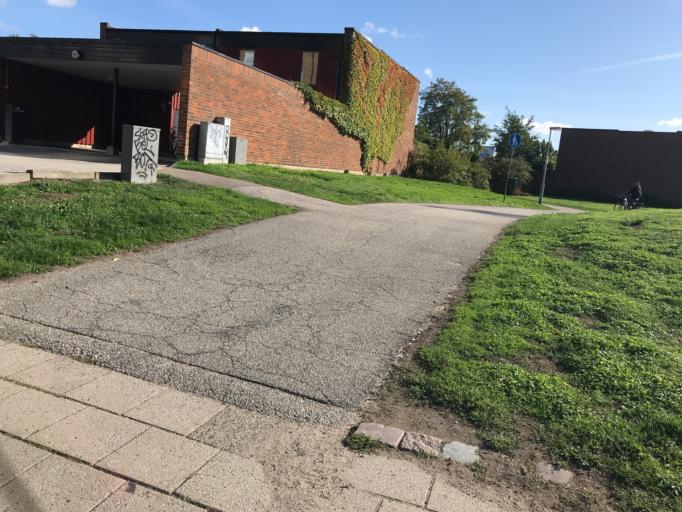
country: SE
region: Skane
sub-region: Malmo
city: Malmoe
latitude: 55.5770
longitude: 13.0008
